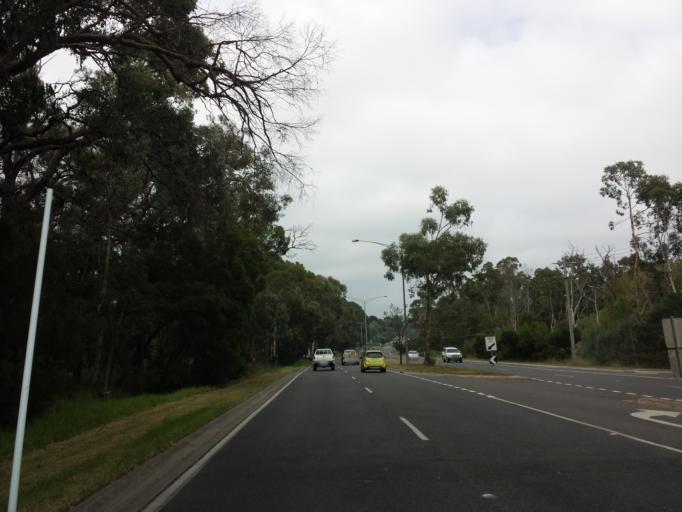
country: AU
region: Victoria
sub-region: Yarra Ranges
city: Montrose
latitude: -37.8047
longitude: 145.3552
